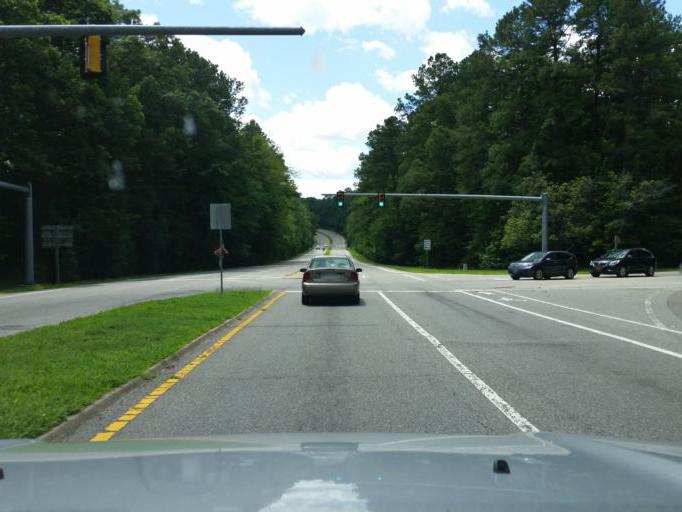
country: US
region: Virginia
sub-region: City of Williamsburg
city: Williamsburg
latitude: 37.2964
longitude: -76.6862
